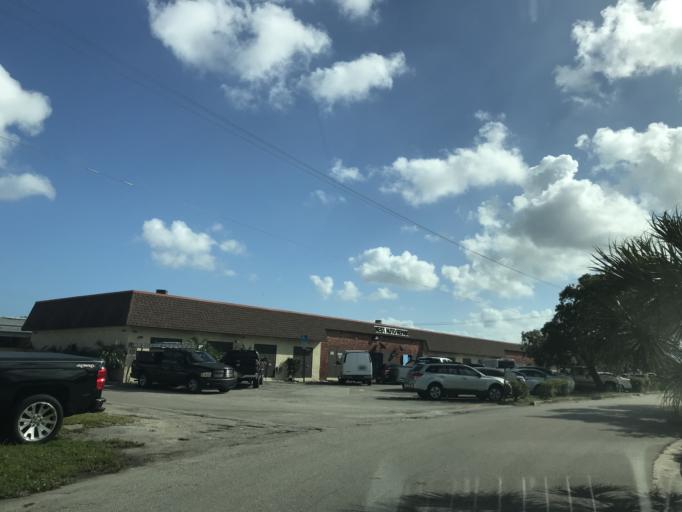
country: US
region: Florida
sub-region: Broward County
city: Margate
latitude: 26.2497
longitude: -80.1954
